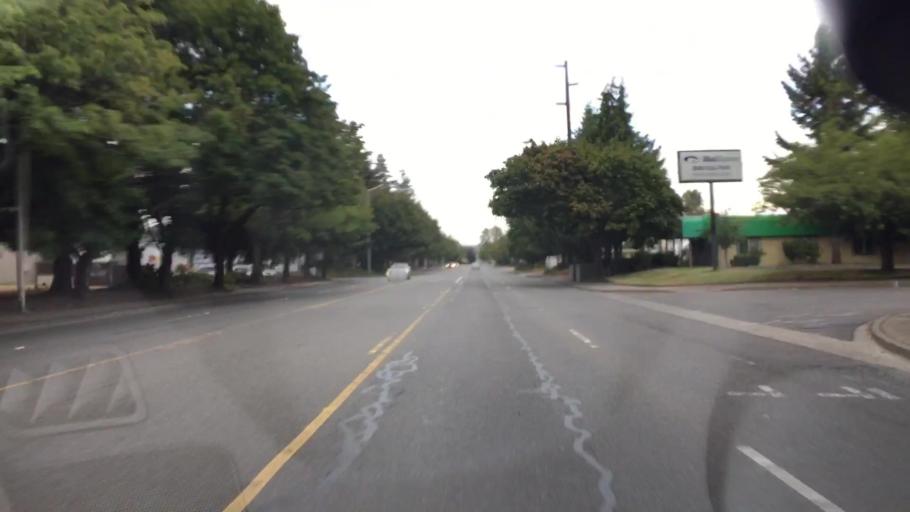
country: US
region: Washington
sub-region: King County
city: Kent
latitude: 47.4273
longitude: -122.2280
